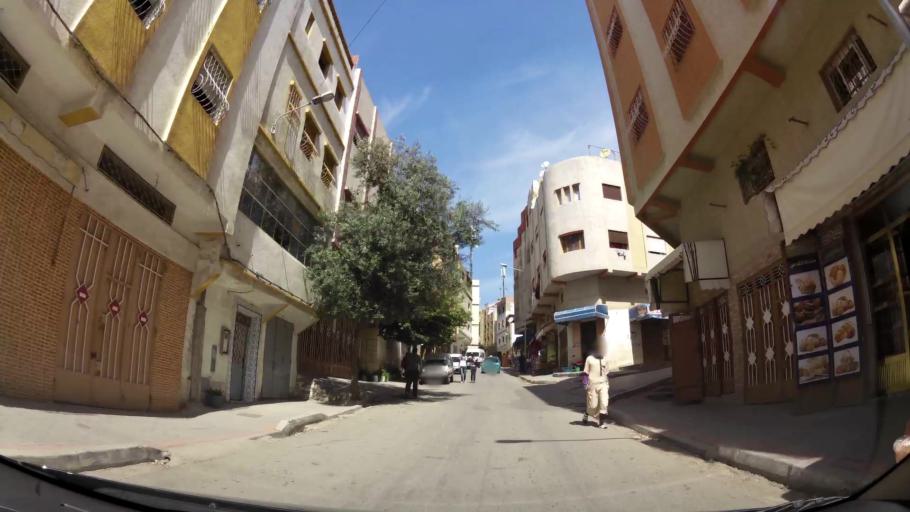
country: MA
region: Tanger-Tetouan
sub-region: Tanger-Assilah
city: Tangier
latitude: 35.7383
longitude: -5.8089
